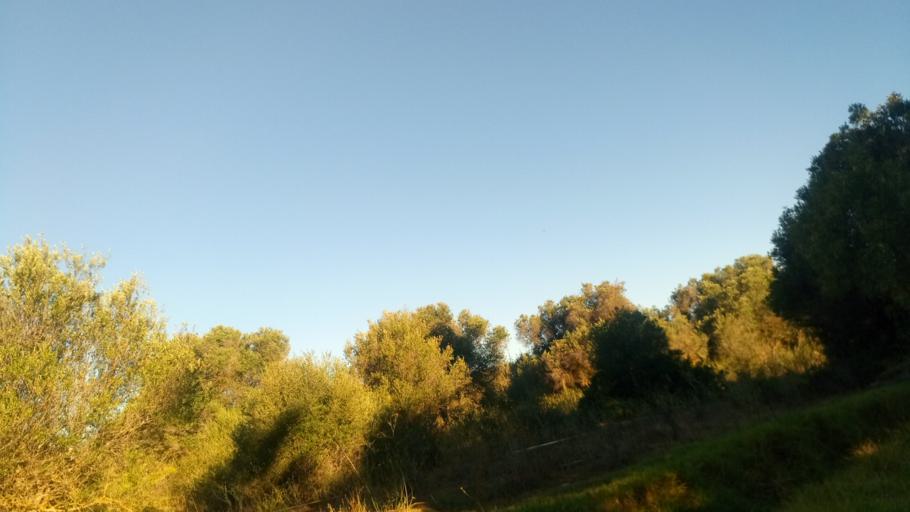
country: PT
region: Faro
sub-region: Tavira
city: Tavira
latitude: 37.1361
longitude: -7.6043
